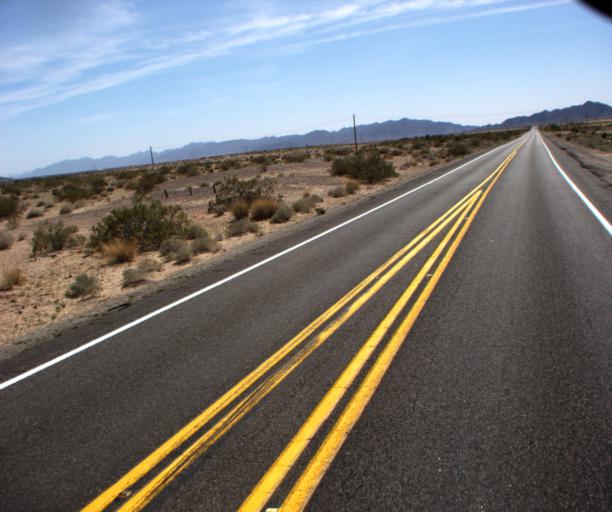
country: US
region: Arizona
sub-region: Yuma County
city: Fortuna Foothills
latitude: 32.8570
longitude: -114.3608
